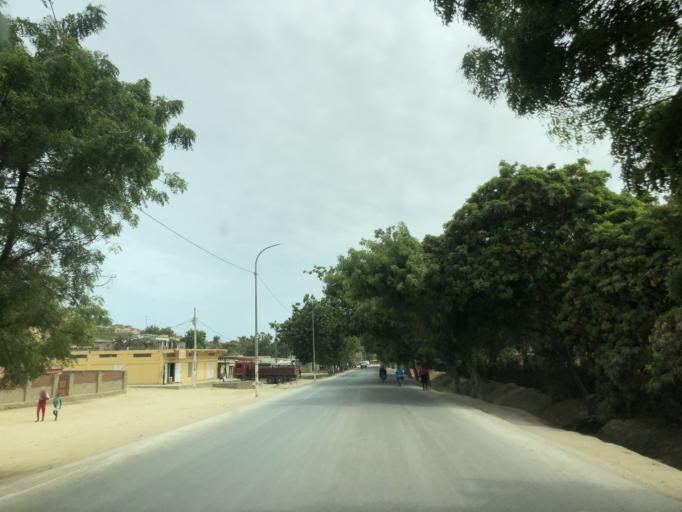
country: AO
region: Cuanza Sul
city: Sumbe
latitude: -11.2186
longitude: 13.8476
